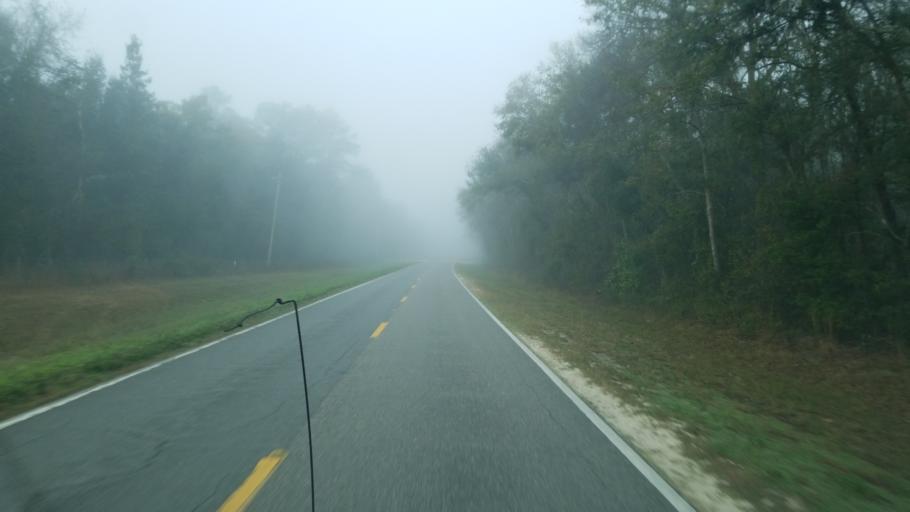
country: US
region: Florida
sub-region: Alachua County
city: High Springs
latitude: 29.9529
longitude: -82.5747
